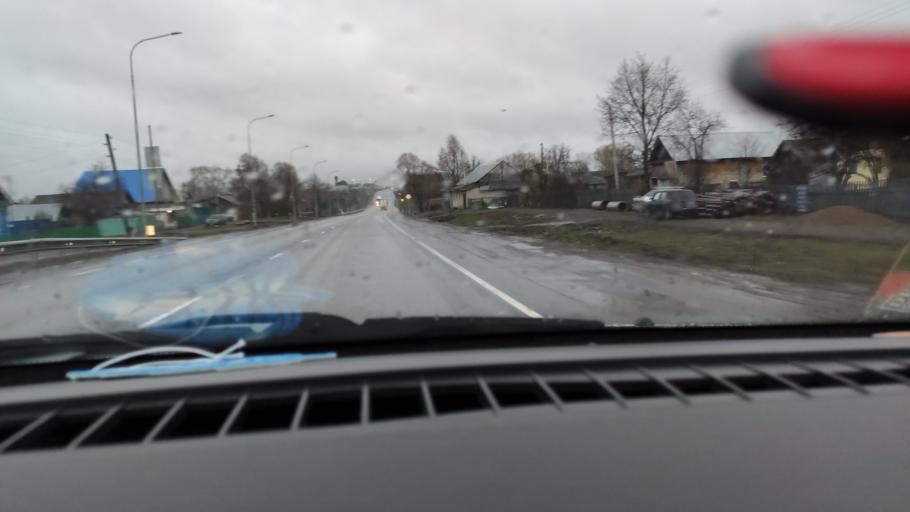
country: RU
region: Tatarstan
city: Mendeleyevsk
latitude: 56.0310
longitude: 52.3763
